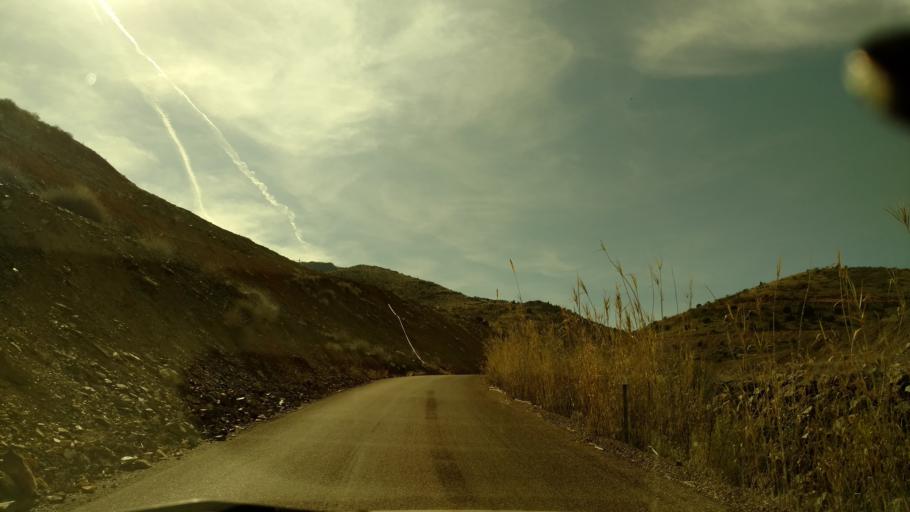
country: US
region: Arizona
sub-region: Yavapai County
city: Clarkdale
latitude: 34.7570
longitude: -112.1262
